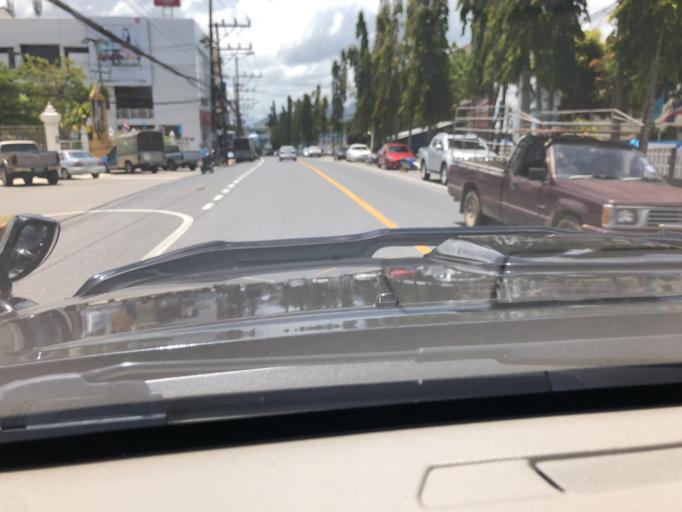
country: TH
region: Krabi
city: Krabi
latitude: 8.0601
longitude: 98.9185
